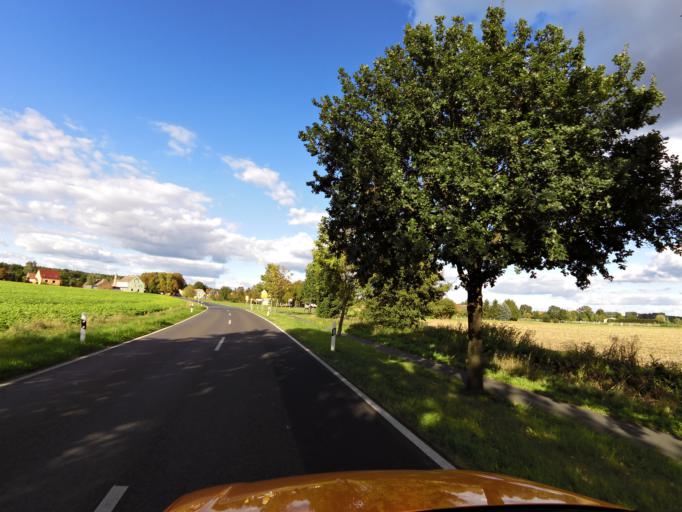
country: DE
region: Brandenburg
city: Luckenwalde
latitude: 52.1241
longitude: 13.1665
